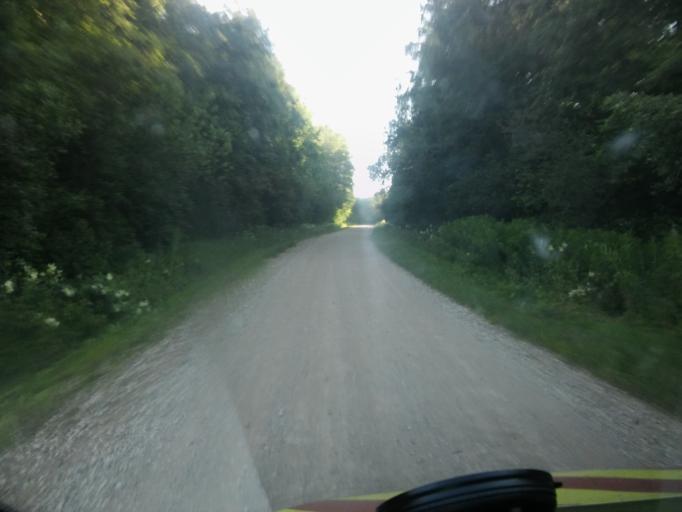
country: EE
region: Valgamaa
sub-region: Torva linn
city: Torva
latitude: 58.0764
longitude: 25.9046
